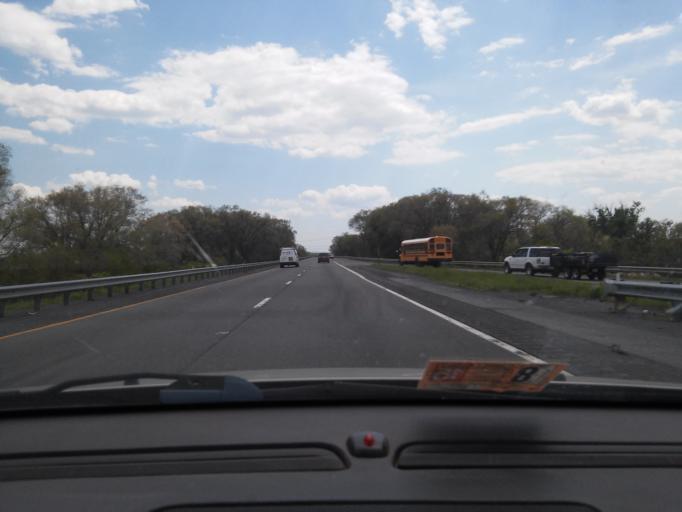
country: US
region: Virginia
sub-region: City of Winchester
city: Winchester
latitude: 39.2154
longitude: -78.1377
